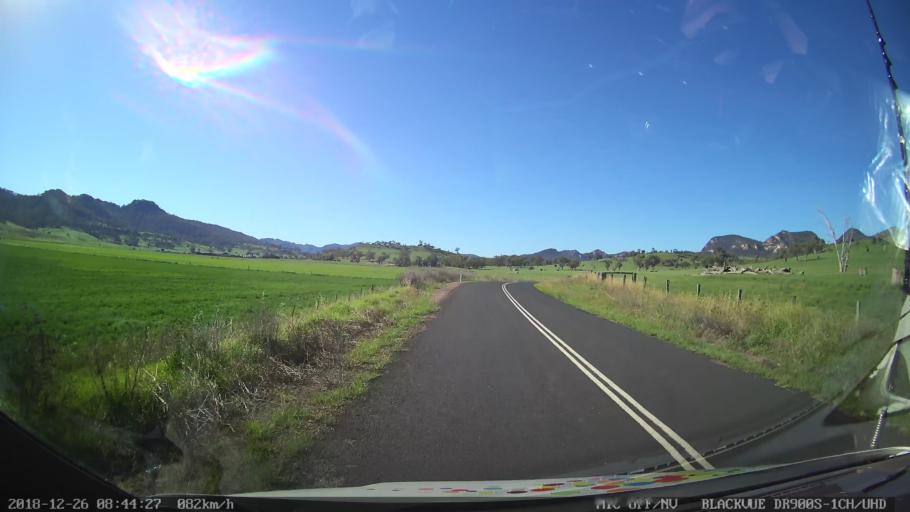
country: AU
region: New South Wales
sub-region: Mid-Western Regional
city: Kandos
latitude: -32.5148
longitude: 150.0808
